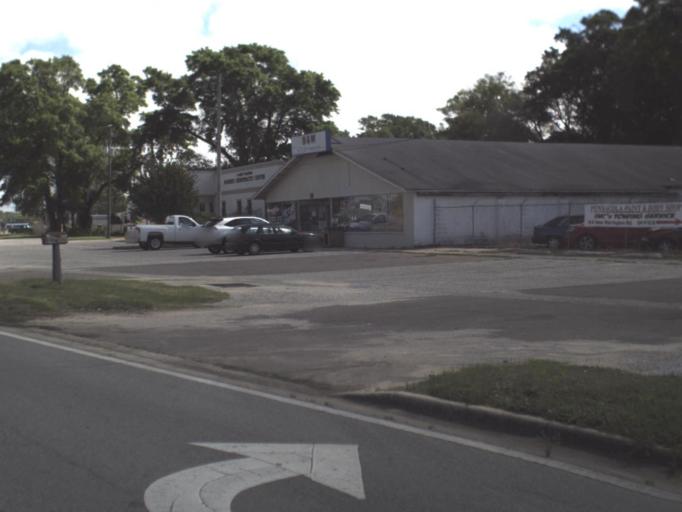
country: US
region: Florida
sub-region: Escambia County
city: West Pensacola
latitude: 30.4217
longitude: -87.2749
